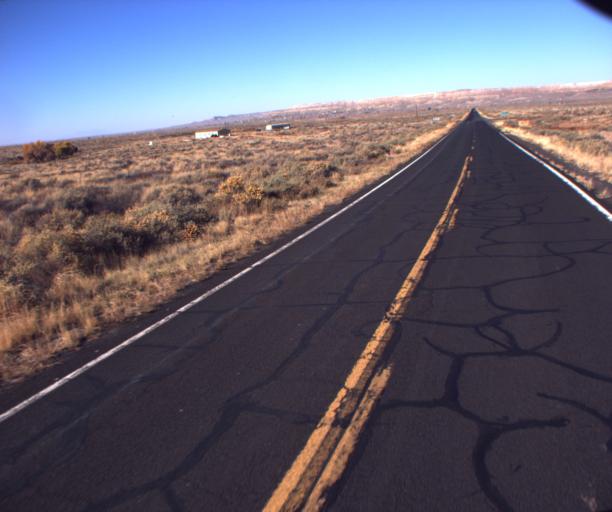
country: US
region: Arizona
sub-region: Navajo County
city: First Mesa
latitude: 35.8388
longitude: -110.3055
